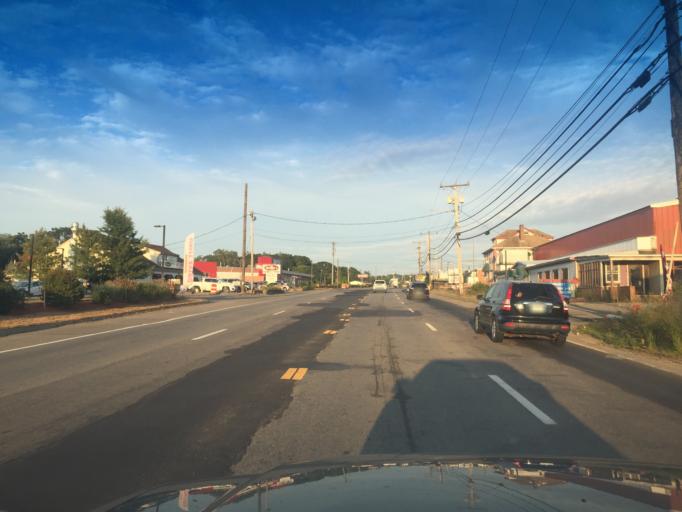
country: US
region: Massachusetts
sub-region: Plymouth County
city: Onset
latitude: 41.7569
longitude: -70.6536
